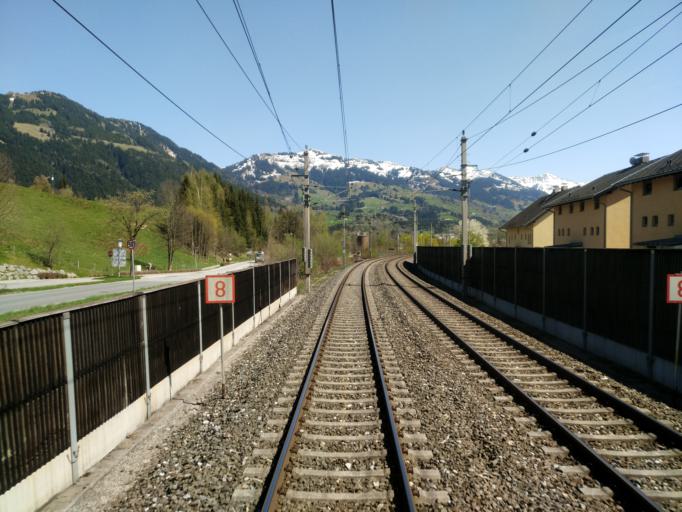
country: AT
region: Tyrol
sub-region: Politischer Bezirk Kitzbuhel
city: Kitzbuhel
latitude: 47.4510
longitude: 12.3778
